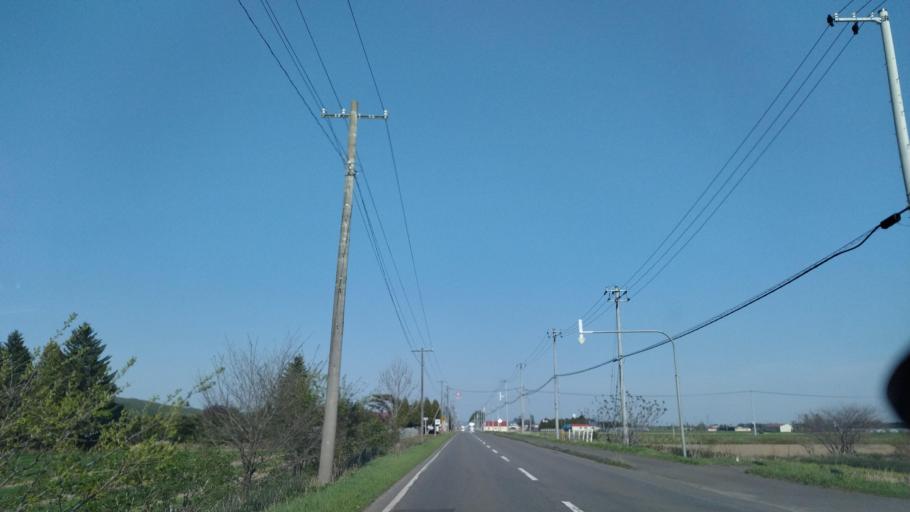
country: JP
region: Hokkaido
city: Obihiro
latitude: 42.9435
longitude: 143.0846
